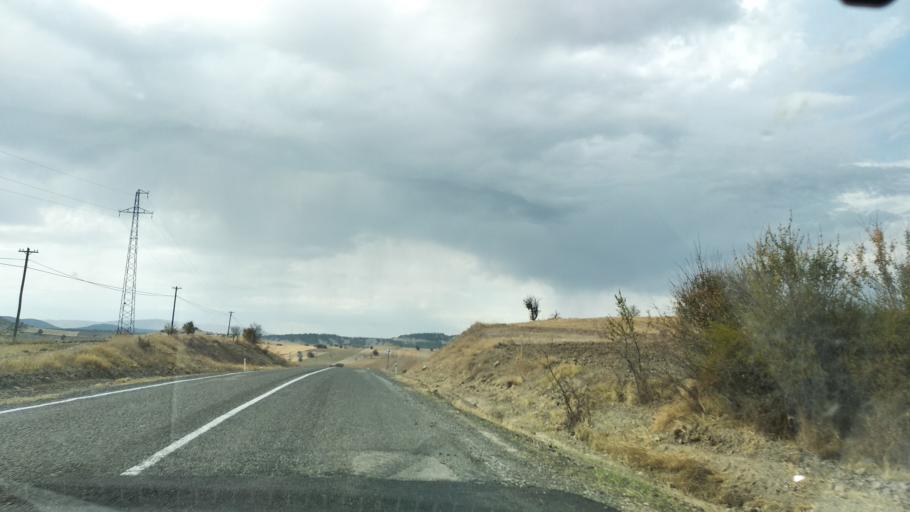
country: TR
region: Bolu
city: Seben
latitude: 40.3719
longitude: 31.5101
